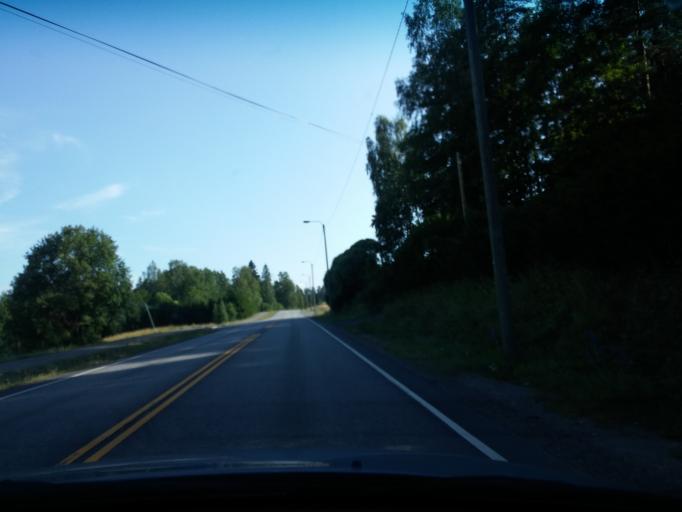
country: FI
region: Uusimaa
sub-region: Porvoo
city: Askola
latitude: 60.5152
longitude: 25.5784
